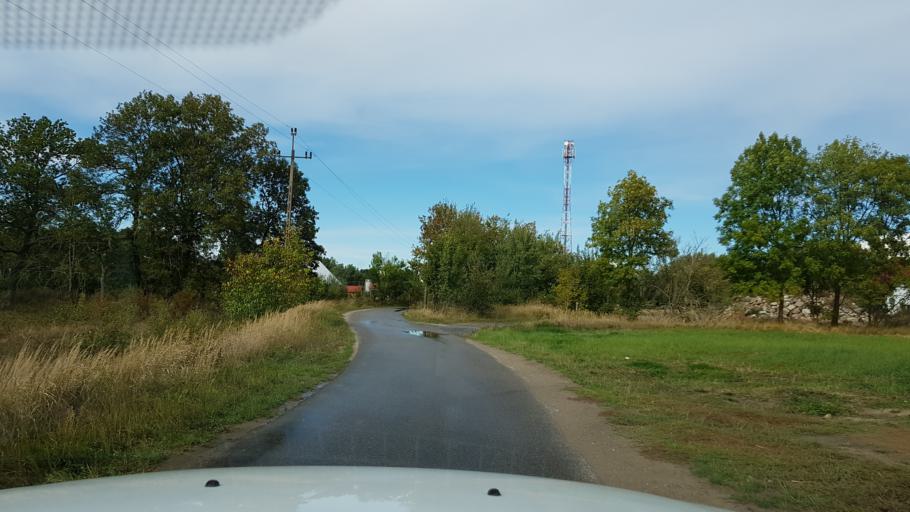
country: PL
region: West Pomeranian Voivodeship
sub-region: Powiat gryfinski
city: Banie
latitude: 53.1055
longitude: 14.6589
